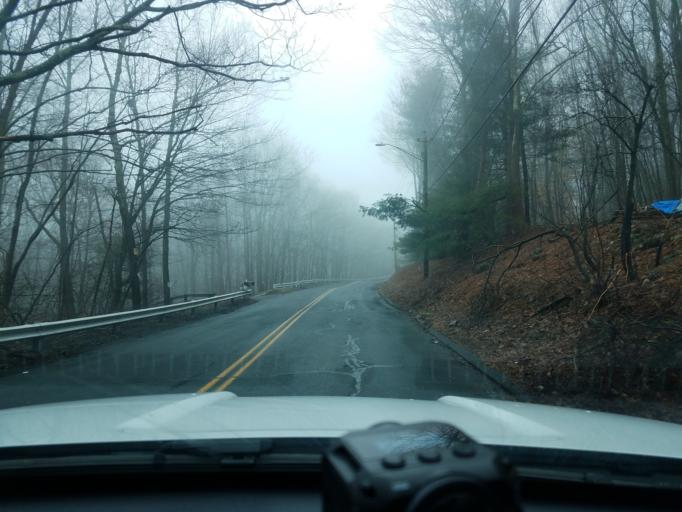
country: US
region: Connecticut
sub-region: New Haven County
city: Naugatuck
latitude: 41.5041
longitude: -73.0219
